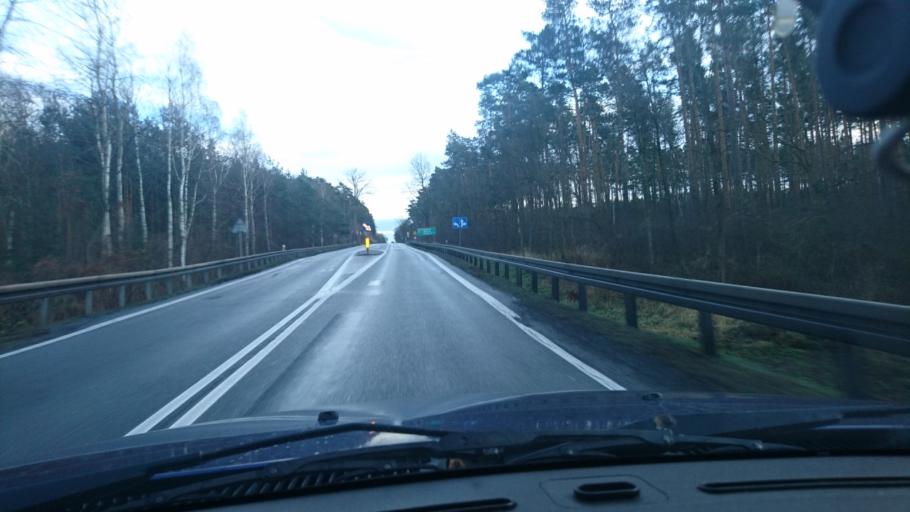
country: PL
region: Greater Poland Voivodeship
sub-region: Powiat kepinski
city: Kepno
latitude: 51.3271
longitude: 17.9628
